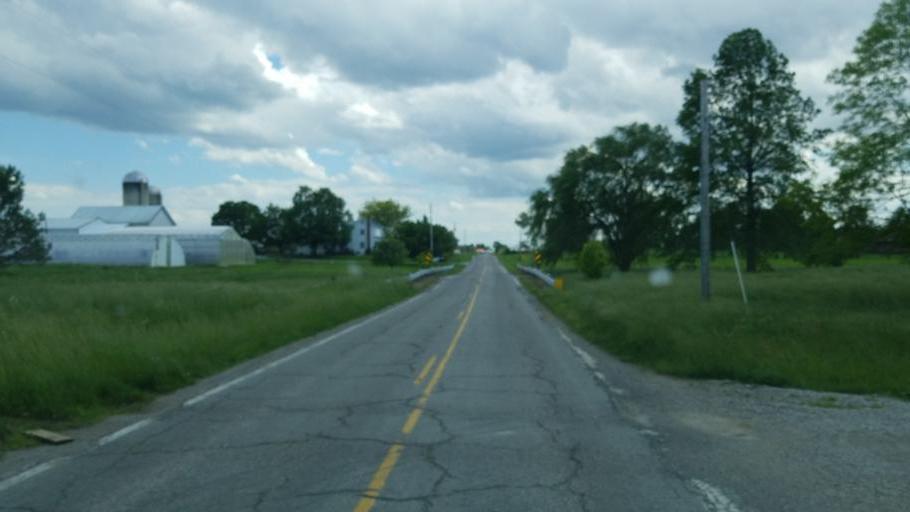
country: US
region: Ohio
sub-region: Huron County
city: Plymouth
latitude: 41.0021
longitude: -82.6065
